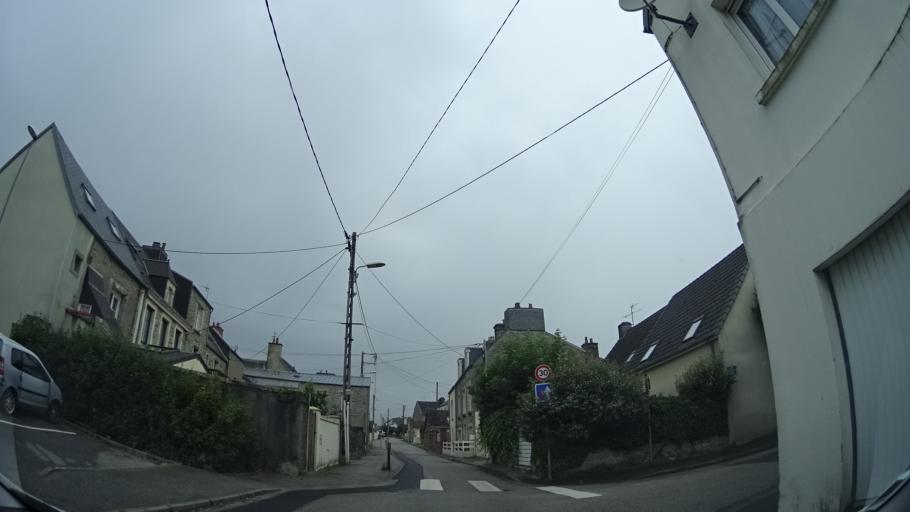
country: FR
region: Lower Normandy
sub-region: Departement de la Manche
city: Octeville
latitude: 49.6318
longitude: -1.6334
